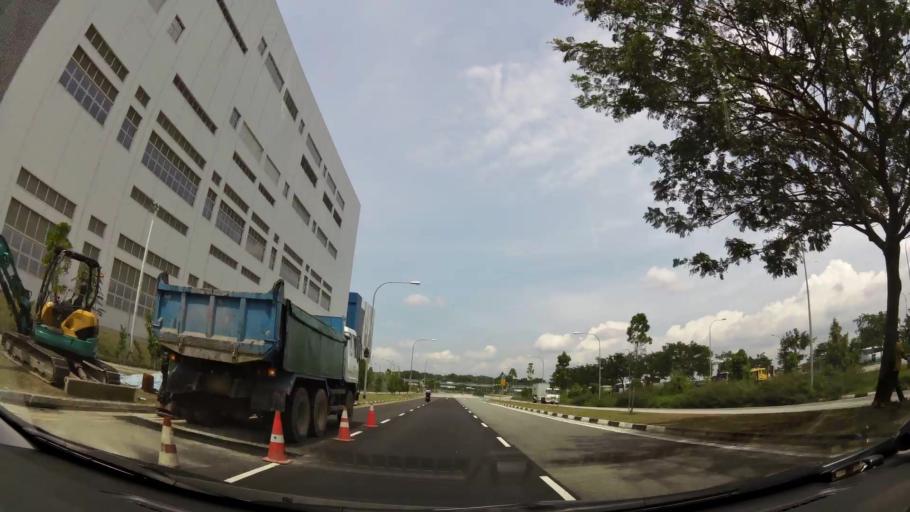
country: MY
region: Johor
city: Johor Bahru
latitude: 1.3556
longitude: 103.7091
